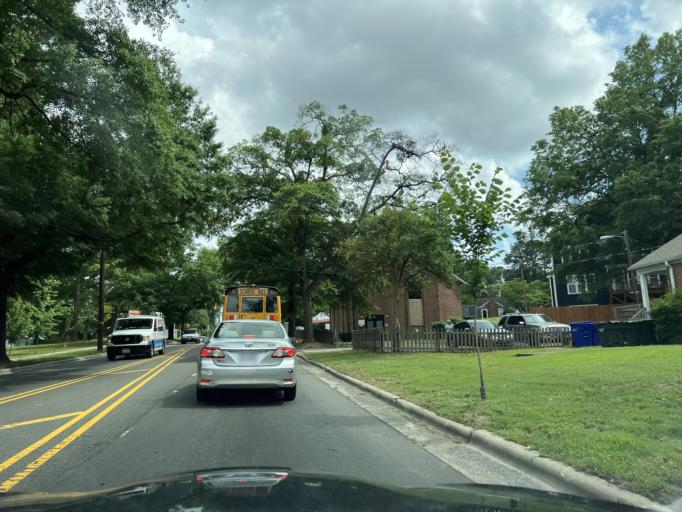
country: US
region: North Carolina
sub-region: Durham County
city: Durham
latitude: 36.0096
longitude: -78.8862
